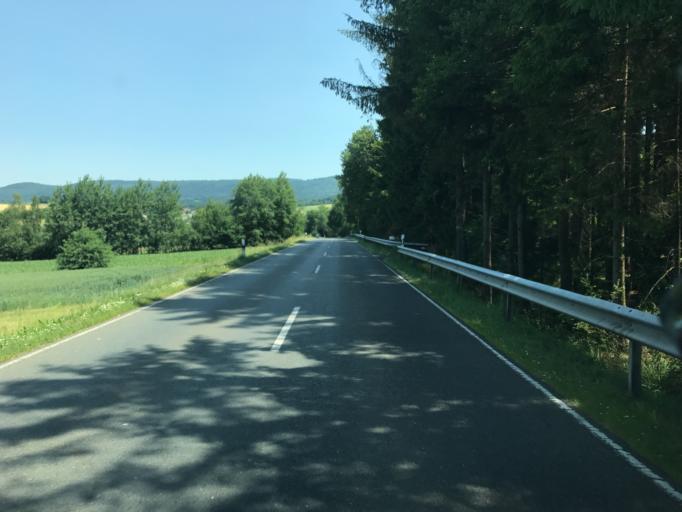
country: DE
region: Bavaria
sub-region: Upper Palatinate
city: Waldmunchen
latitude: 49.3546
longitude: 12.6861
